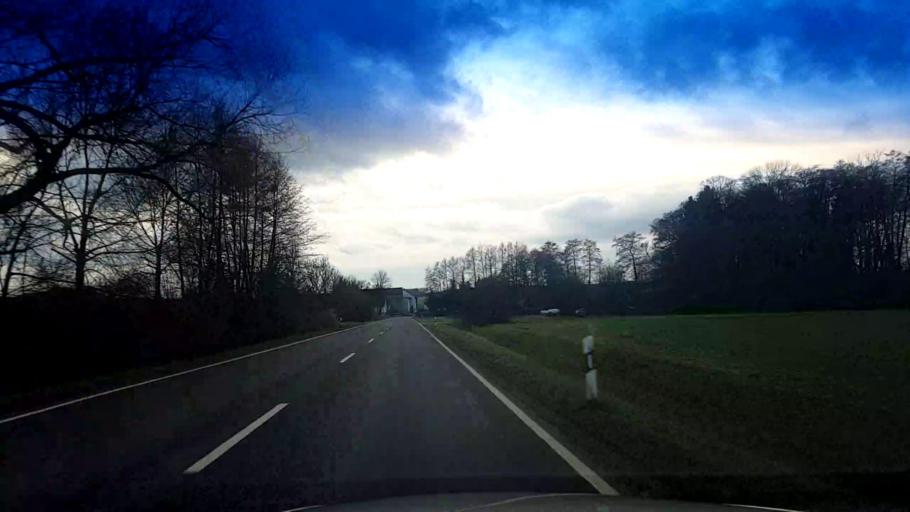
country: DE
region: Bavaria
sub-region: Upper Franconia
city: Strullendorf
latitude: 49.8598
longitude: 11.0138
